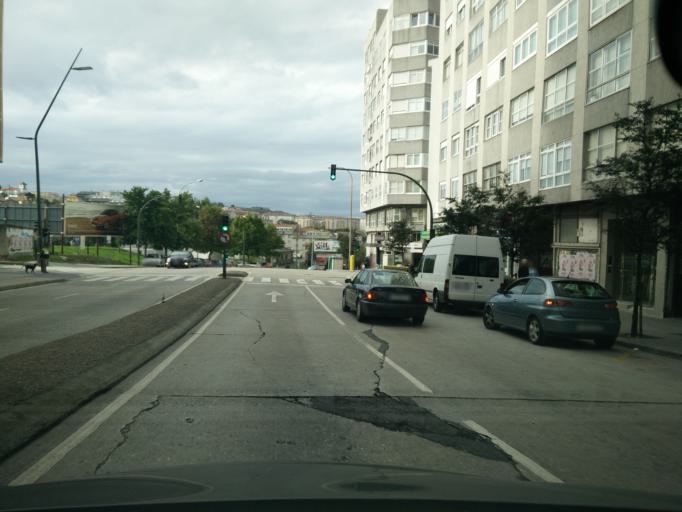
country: ES
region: Galicia
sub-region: Provincia da Coruna
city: A Coruna
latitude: 43.3649
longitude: -8.4241
